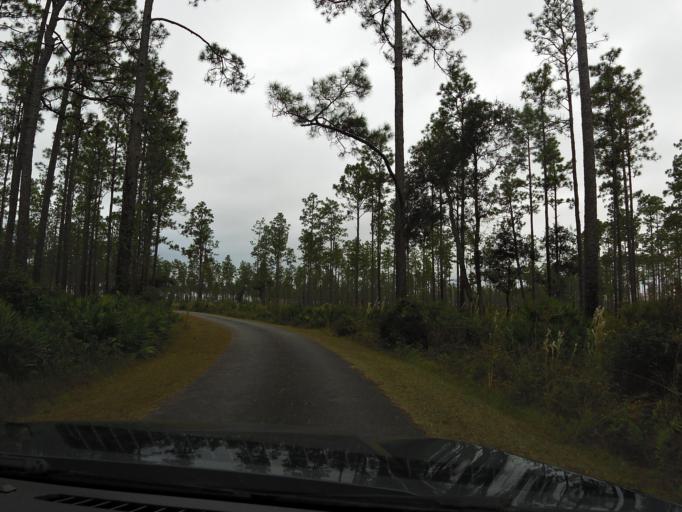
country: US
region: Georgia
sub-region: Charlton County
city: Folkston
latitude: 30.7104
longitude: -82.1621
